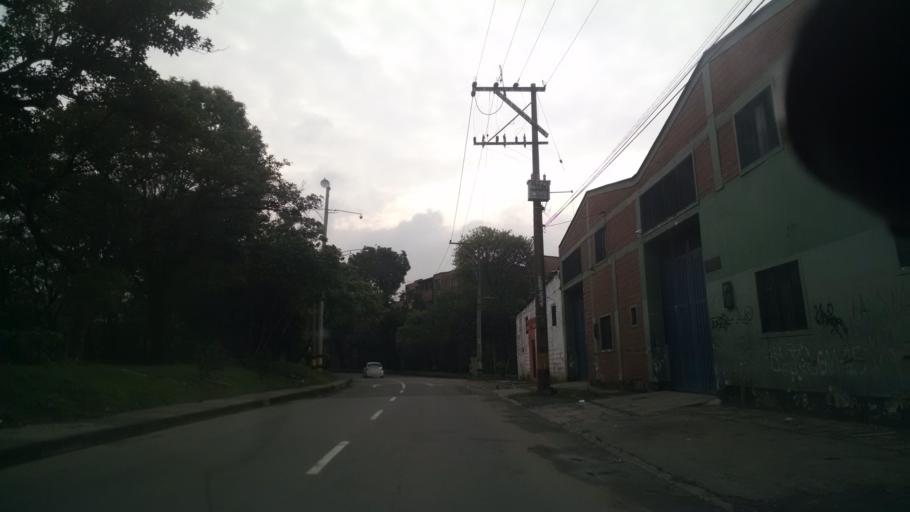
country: CO
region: Antioquia
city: Medellin
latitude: 6.2520
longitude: -75.5812
